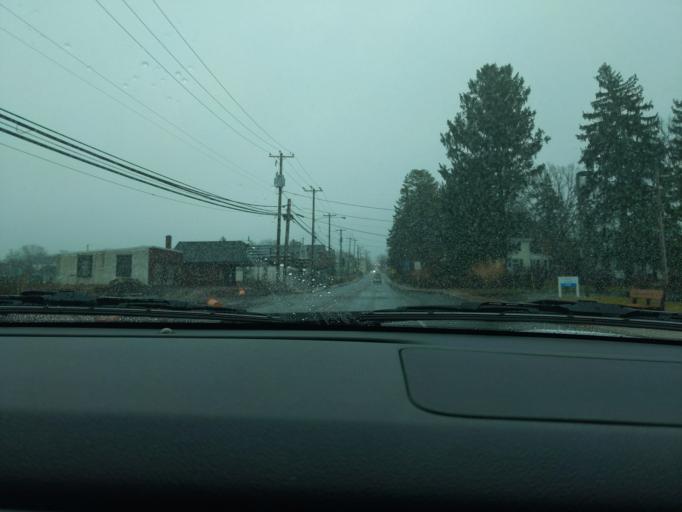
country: US
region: Pennsylvania
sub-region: Bucks County
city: Dublin
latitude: 40.3739
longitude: -75.2066
